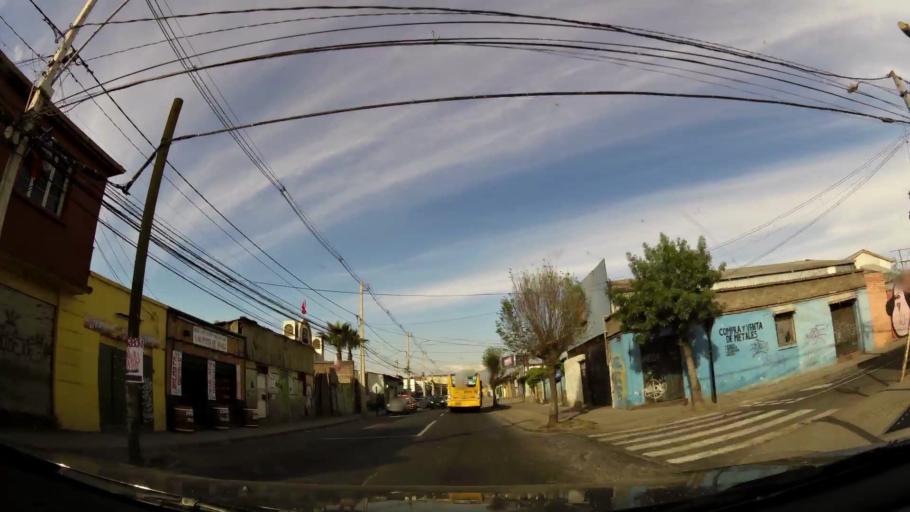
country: CL
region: Santiago Metropolitan
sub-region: Provincia de Cordillera
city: Puente Alto
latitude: -33.6129
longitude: -70.5813
